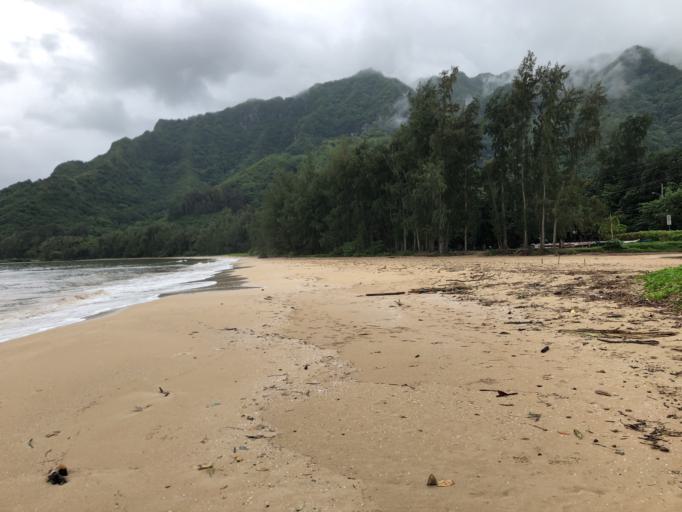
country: US
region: Hawaii
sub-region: Honolulu County
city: Punalu'u
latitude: 21.5565
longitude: -157.8751
